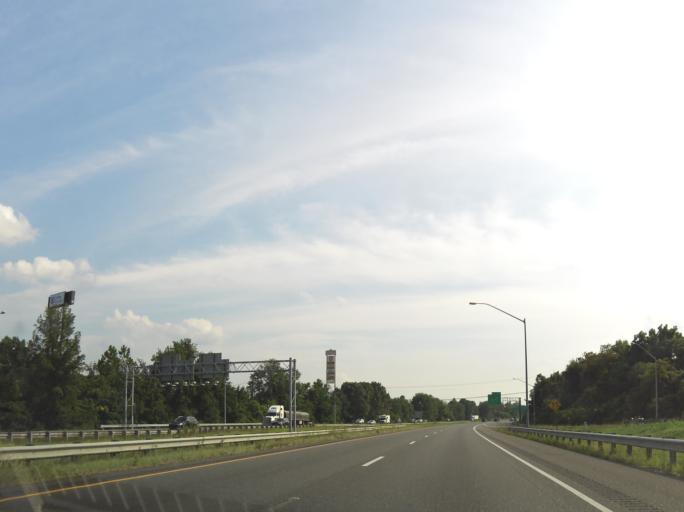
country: US
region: Maryland
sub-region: Washington County
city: Halfway
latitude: 39.6258
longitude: -77.7760
